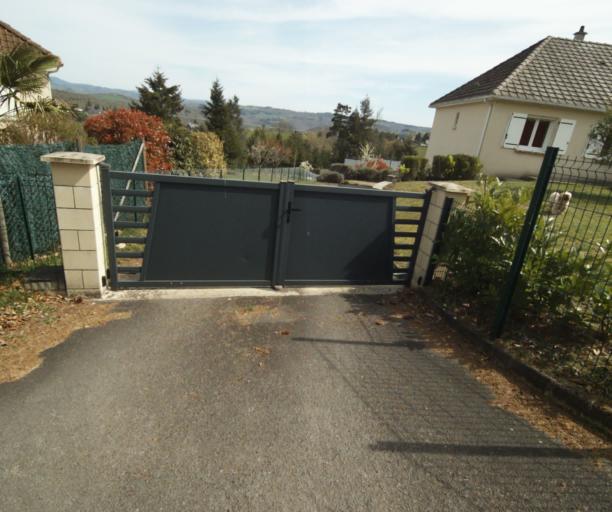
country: FR
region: Limousin
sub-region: Departement de la Correze
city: Naves
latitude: 45.3073
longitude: 1.7660
